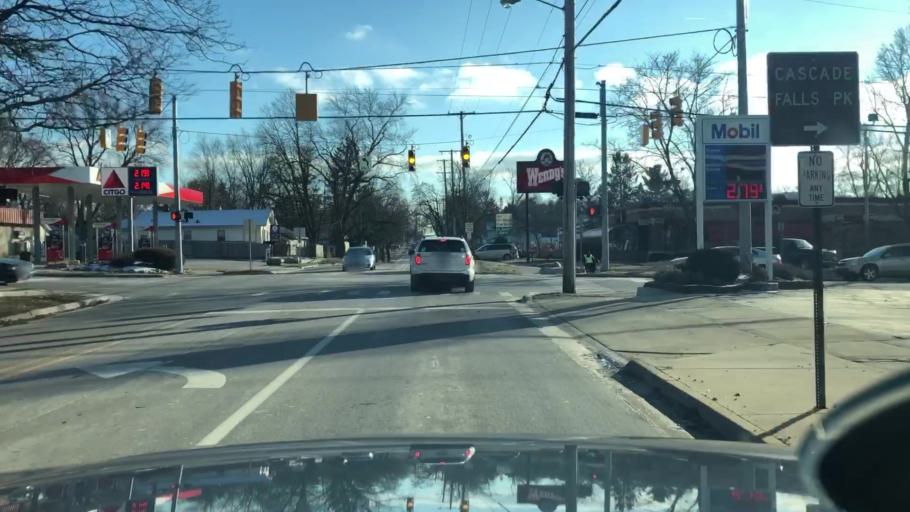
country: US
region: Michigan
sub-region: Jackson County
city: Jackson
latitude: 42.2332
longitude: -84.4233
